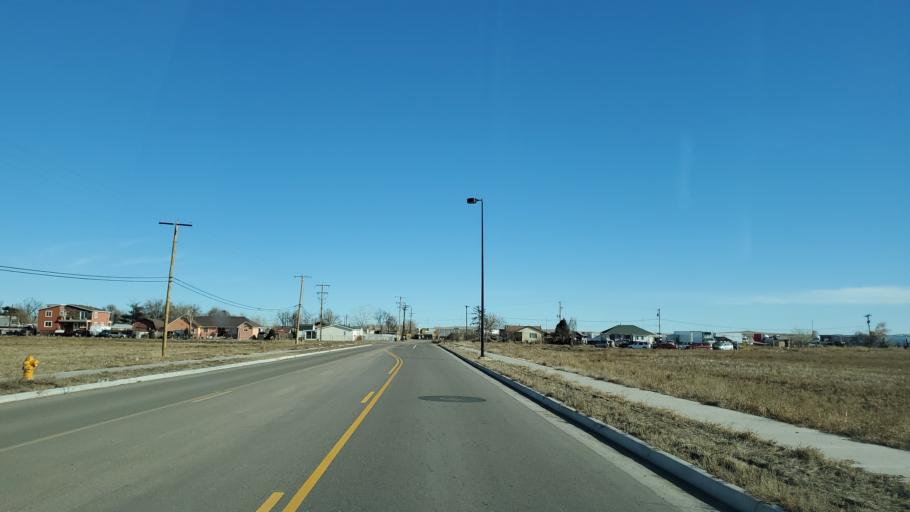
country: US
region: Colorado
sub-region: Adams County
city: Derby
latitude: 39.8490
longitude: -104.8956
